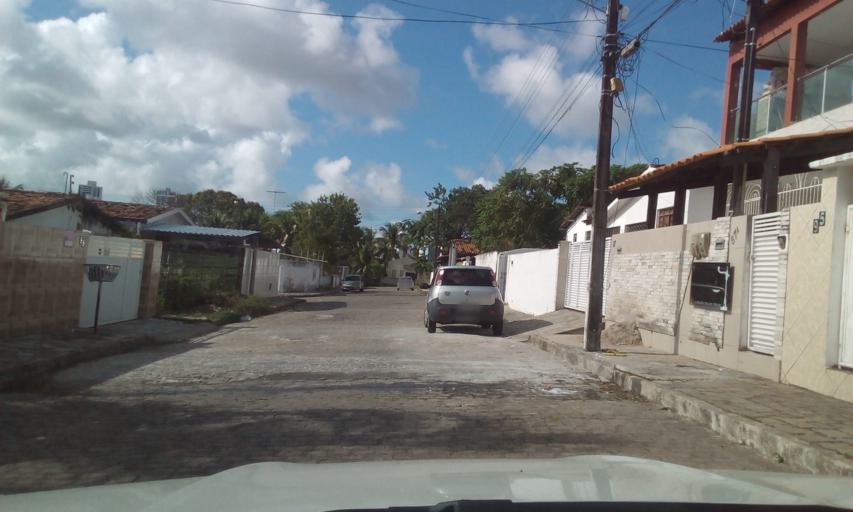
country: BR
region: Paraiba
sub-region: Joao Pessoa
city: Joao Pessoa
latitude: -7.1328
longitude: -34.8523
